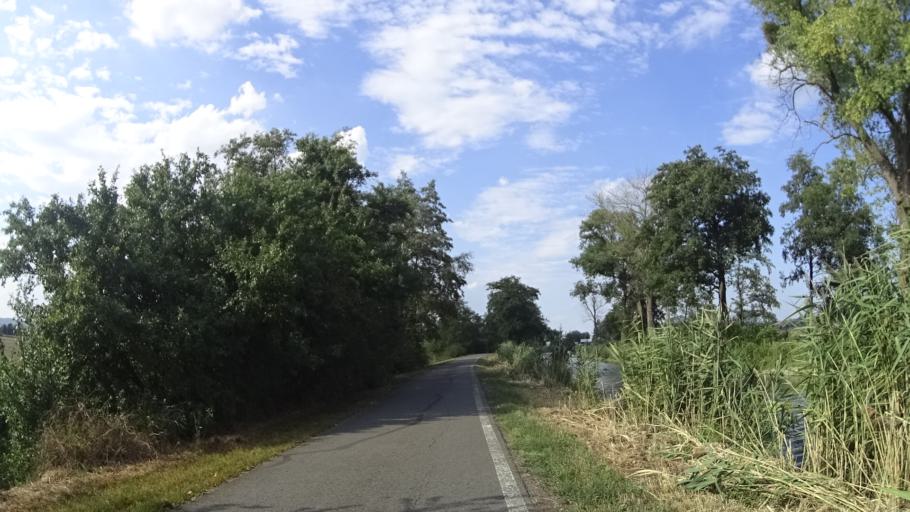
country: CZ
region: Zlin
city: Babice
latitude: 49.0957
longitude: 17.4732
